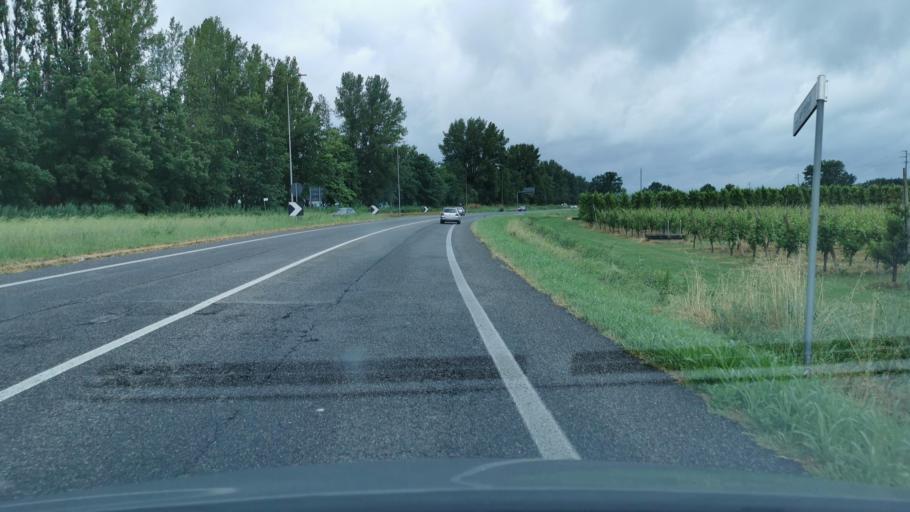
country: IT
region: Emilia-Romagna
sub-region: Provincia di Ravenna
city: Granarolo
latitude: 44.3506
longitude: 11.9271
